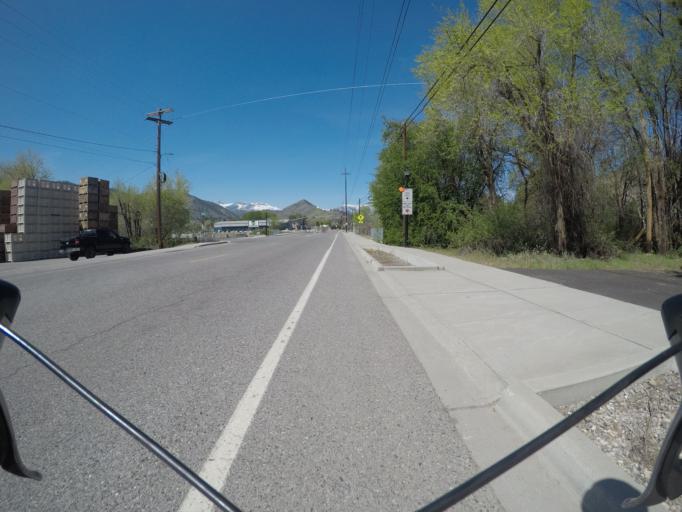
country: US
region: Washington
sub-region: Chelan County
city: Cashmere
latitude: 47.5213
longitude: -120.4766
